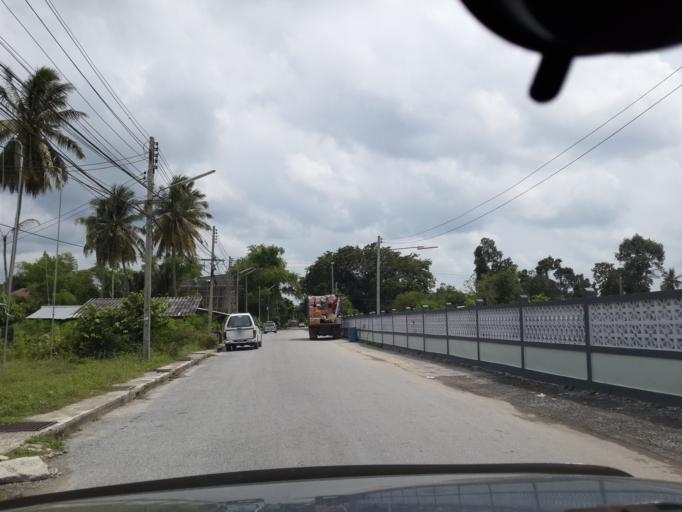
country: TH
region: Pattani
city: Pattani
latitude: 6.8556
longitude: 101.2536
